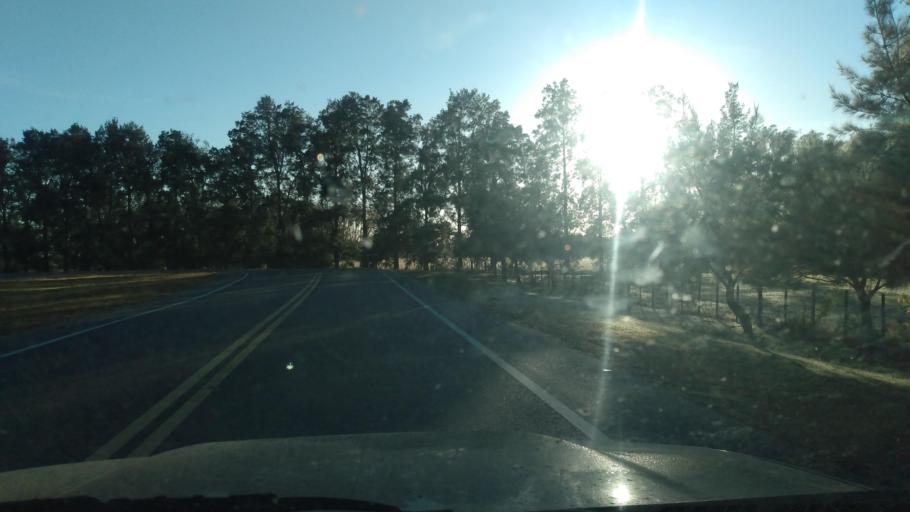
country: AR
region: Buenos Aires
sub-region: Partido de Lujan
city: Lujan
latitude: -34.5369
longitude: -59.2550
